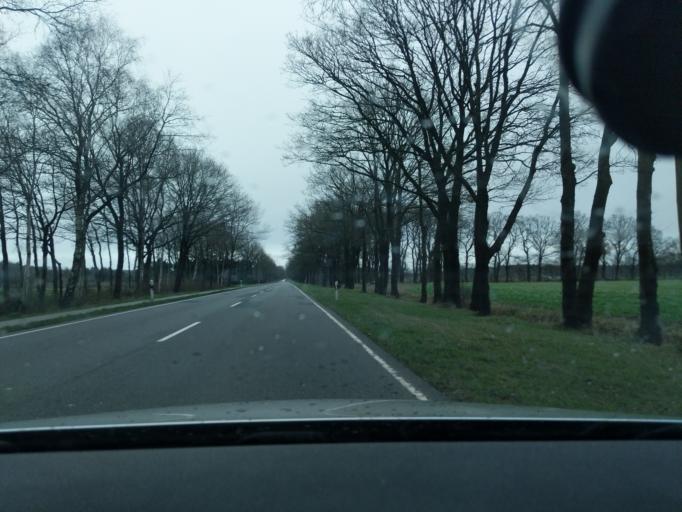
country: DE
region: Lower Saxony
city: Bremervorde
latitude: 53.5055
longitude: 9.1927
